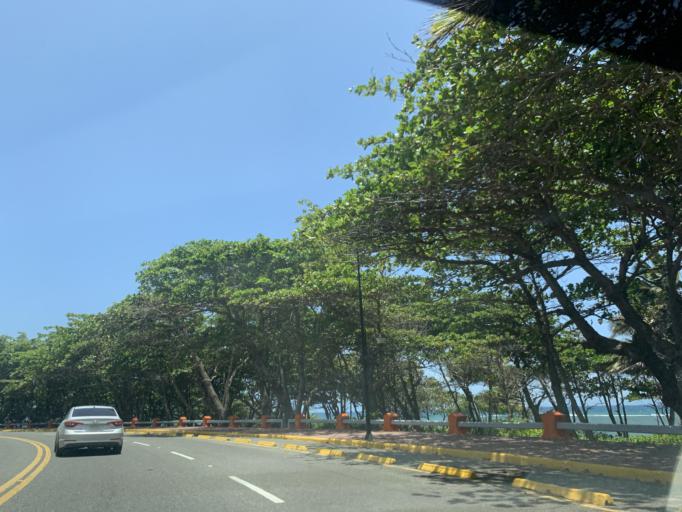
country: DO
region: Puerto Plata
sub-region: Puerto Plata
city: Puerto Plata
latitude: 19.7974
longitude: -70.6855
